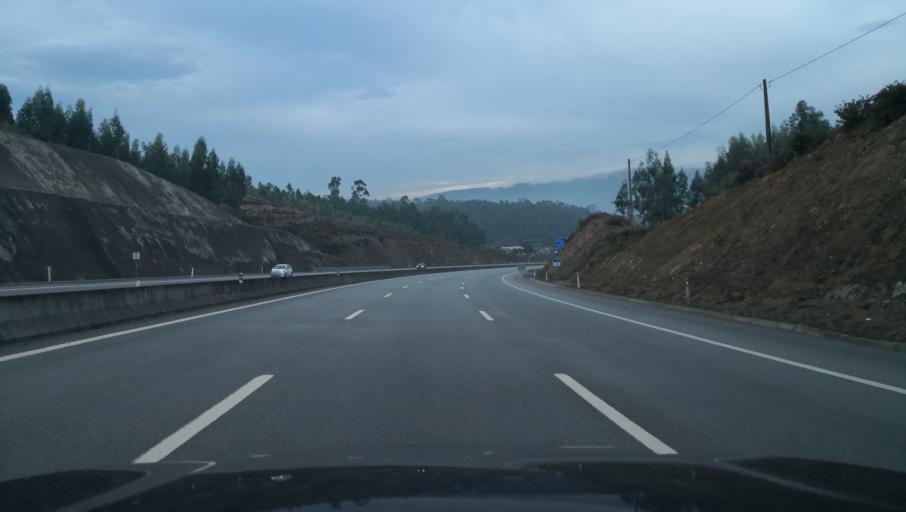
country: PT
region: Porto
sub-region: Paredes
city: Recarei
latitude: 41.1123
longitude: -8.4320
